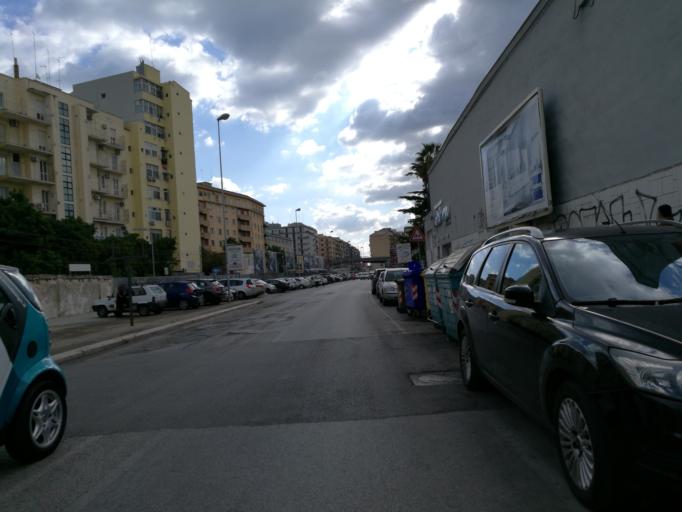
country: IT
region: Apulia
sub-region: Provincia di Bari
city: Bari
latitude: 41.1174
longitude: 16.8853
